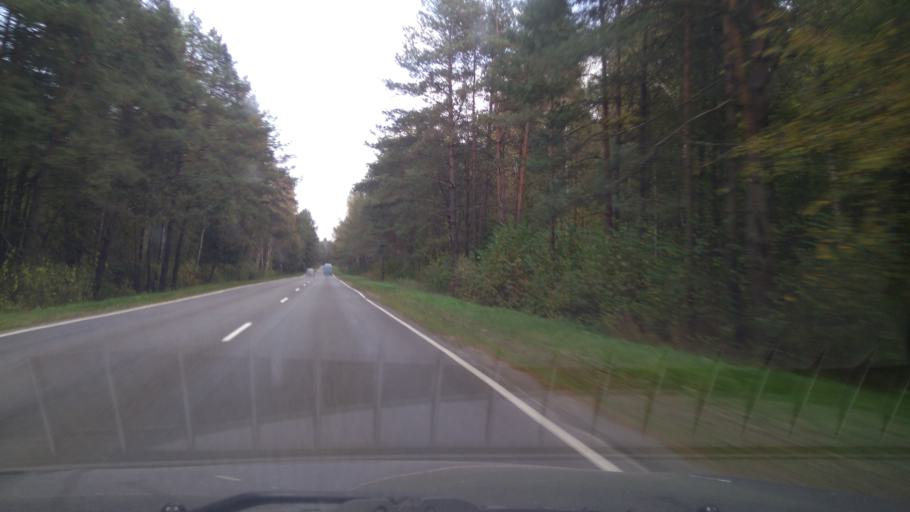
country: BY
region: Minsk
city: Druzhny
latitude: 53.6356
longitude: 27.8947
